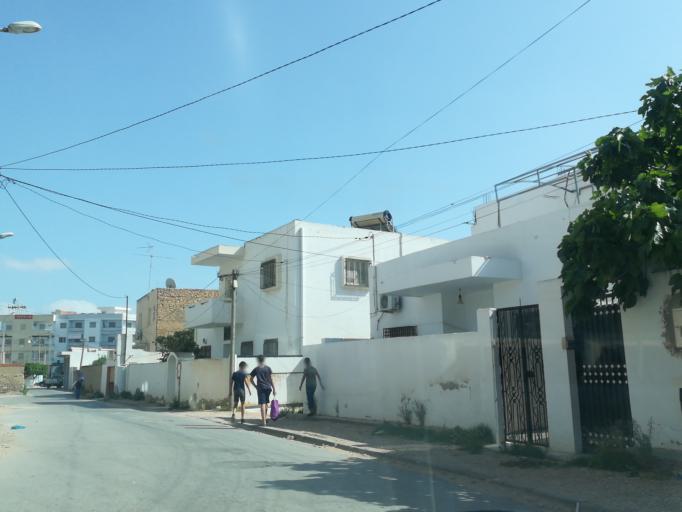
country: TN
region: Safaqis
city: Al Qarmadah
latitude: 34.8047
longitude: 10.7601
